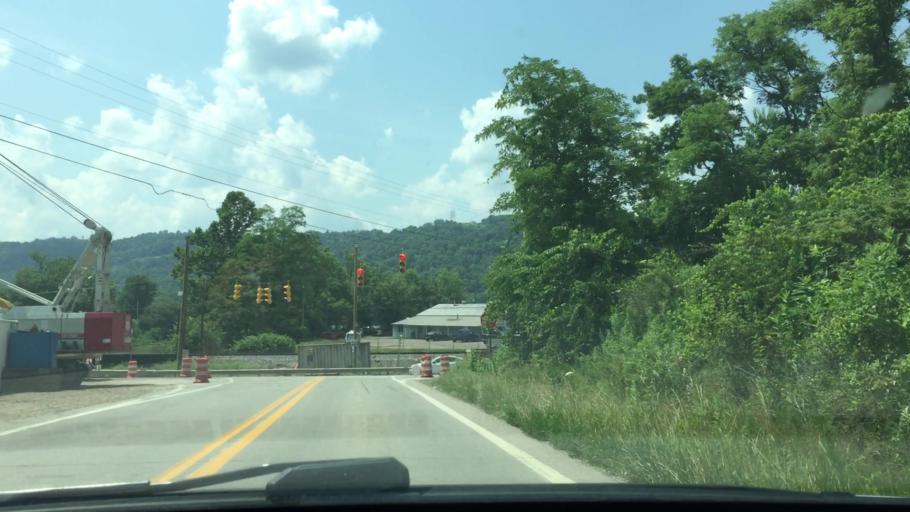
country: US
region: West Virginia
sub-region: Wetzel County
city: New Martinsville
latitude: 39.7093
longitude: -80.8222
